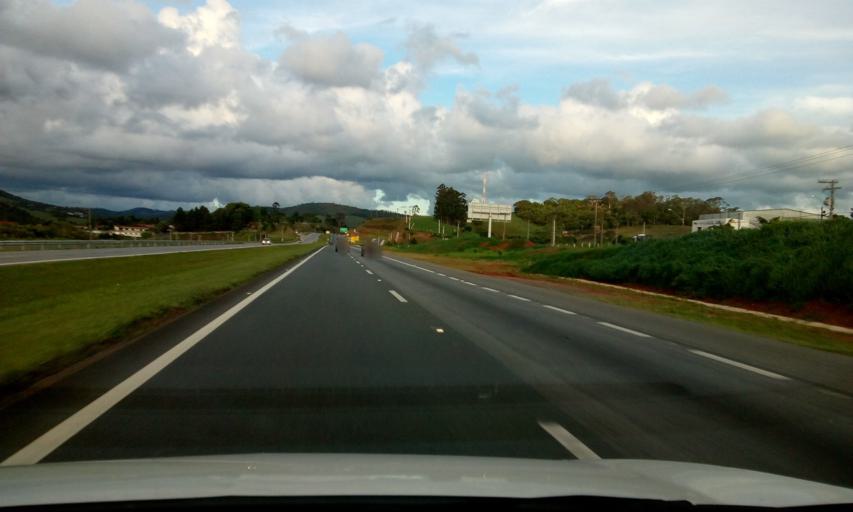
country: BR
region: Sao Paulo
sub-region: Bom Jesus Dos Perdoes
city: Bom Jesus dos Perdoes
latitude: -23.1688
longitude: -46.4155
